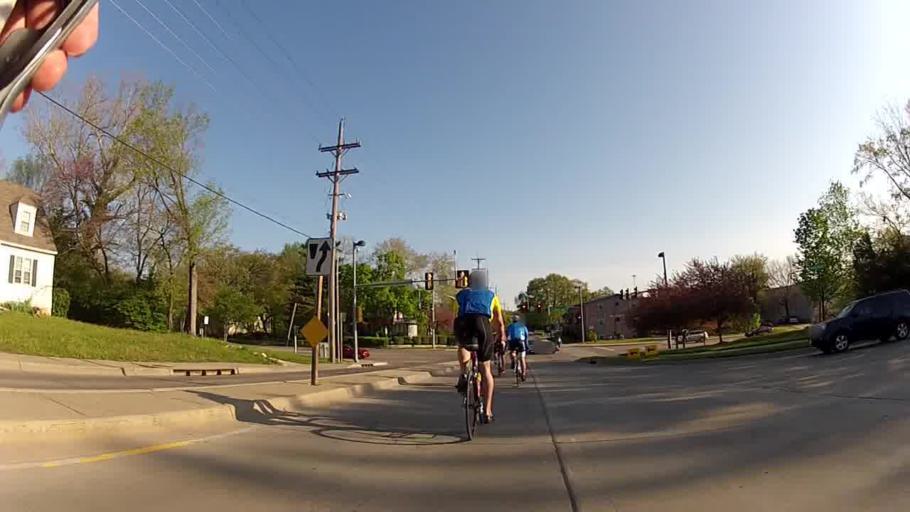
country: US
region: Kansas
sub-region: Riley County
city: Manhattan
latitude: 39.1855
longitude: -96.5888
